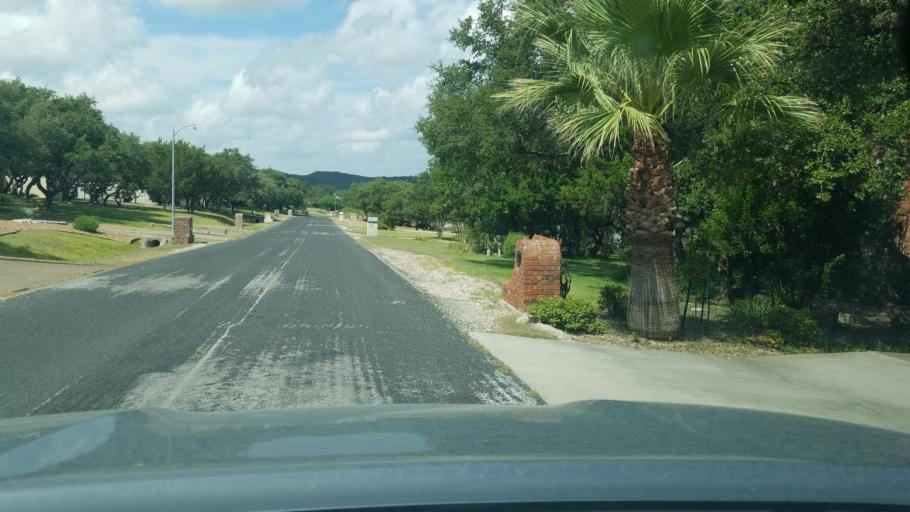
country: US
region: Texas
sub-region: Bexar County
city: Timberwood Park
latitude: 29.6757
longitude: -98.5169
